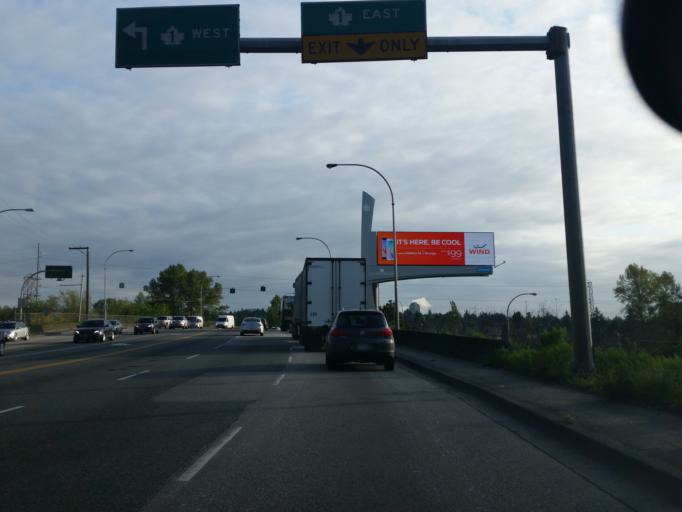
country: CA
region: British Columbia
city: New Westminster
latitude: 49.2318
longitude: -122.8824
